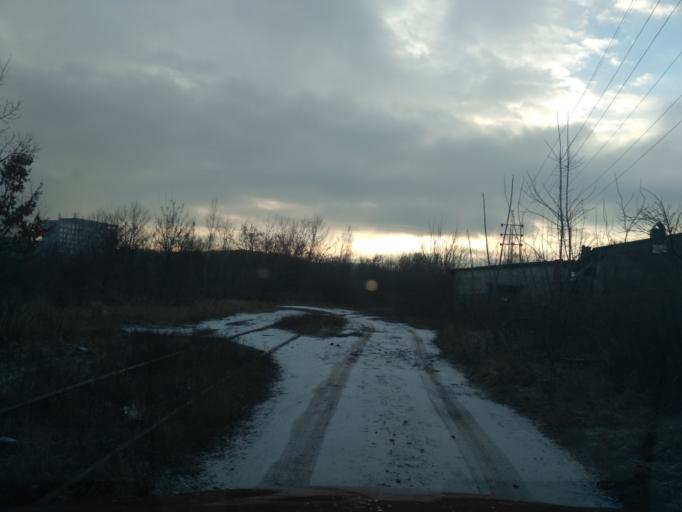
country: SK
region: Kosicky
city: Kosice
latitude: 48.7300
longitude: 21.2672
